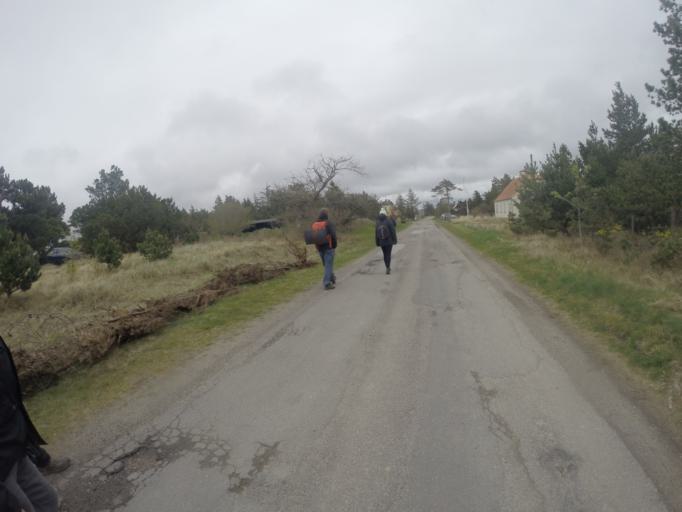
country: DK
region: North Denmark
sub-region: Thisted Kommune
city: Hurup
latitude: 56.8702
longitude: 8.3088
